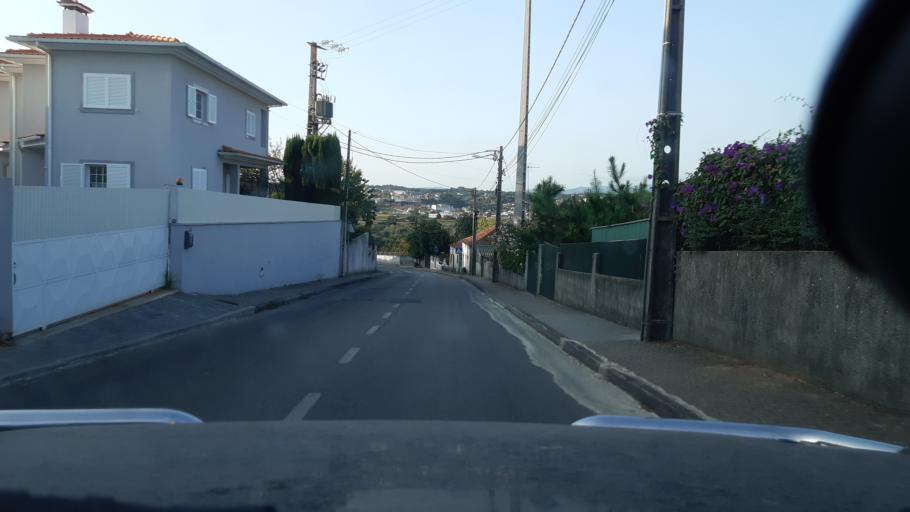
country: PT
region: Aveiro
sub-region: Agueda
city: Agueda
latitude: 40.5564
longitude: -8.4341
